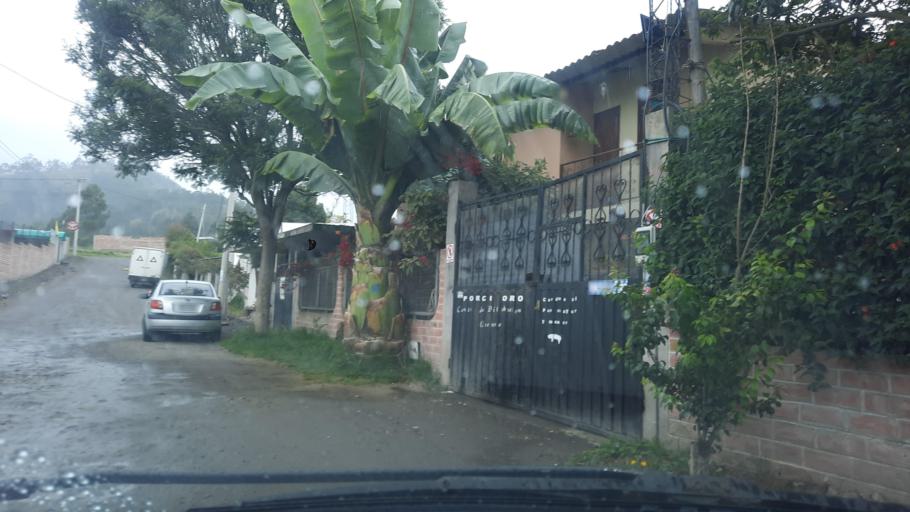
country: EC
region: Chimborazo
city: Riobamba
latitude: -1.6897
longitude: -78.6562
